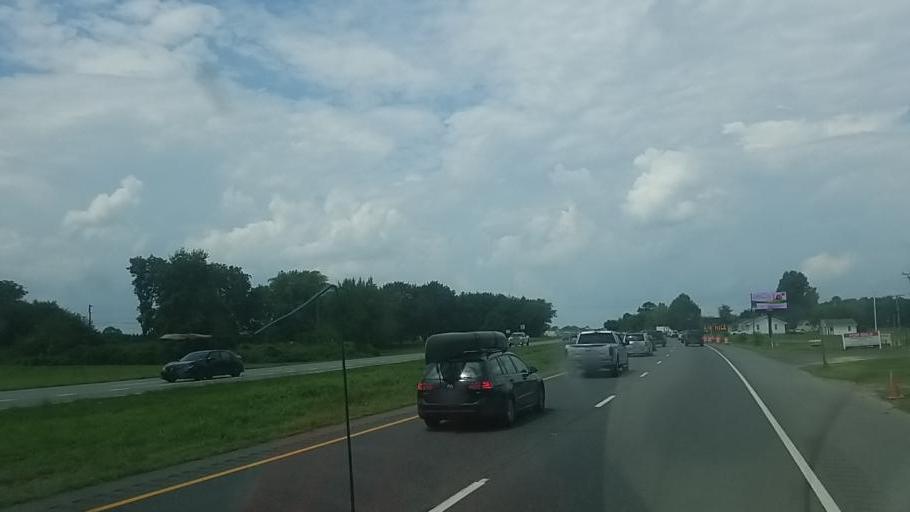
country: US
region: Delaware
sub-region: Sussex County
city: Milford
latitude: 38.9845
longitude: -75.4410
